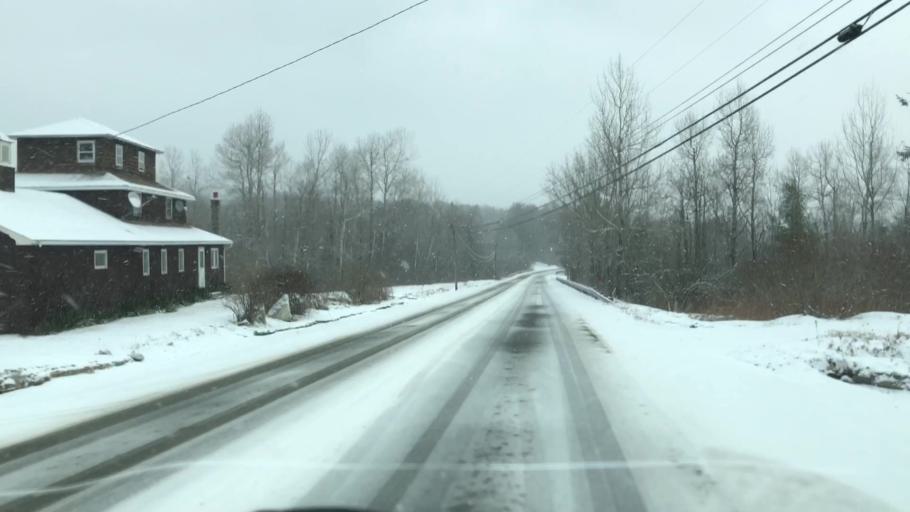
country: US
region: Massachusetts
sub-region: Berkshire County
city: Adams
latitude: 42.5755
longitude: -73.0512
